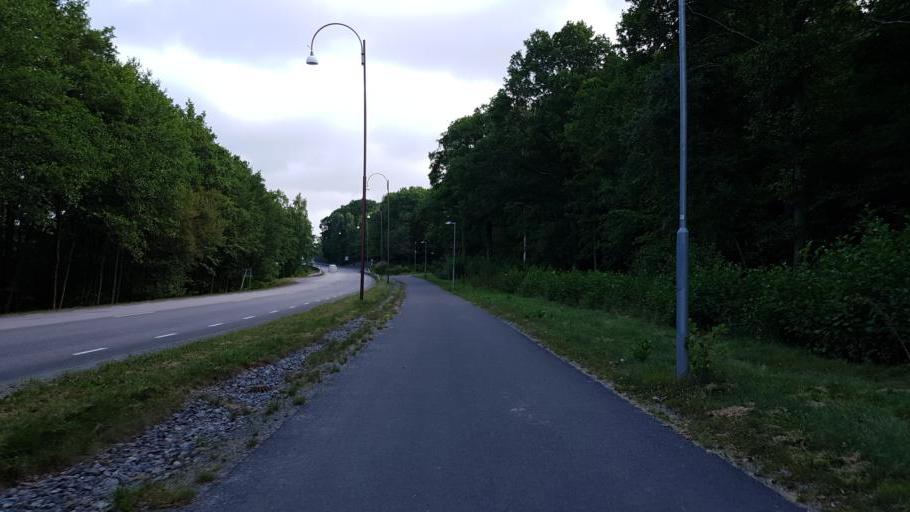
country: SE
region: Vaestra Goetaland
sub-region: Harryda Kommun
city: Molnlycke
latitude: 57.6649
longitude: 12.0924
